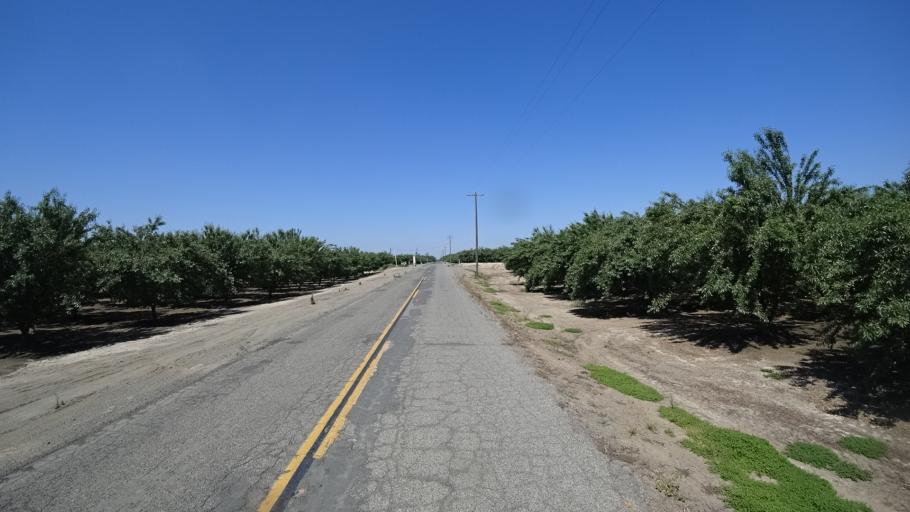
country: US
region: California
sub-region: Fresno County
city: Kingsburg
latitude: 36.4451
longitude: -119.5834
